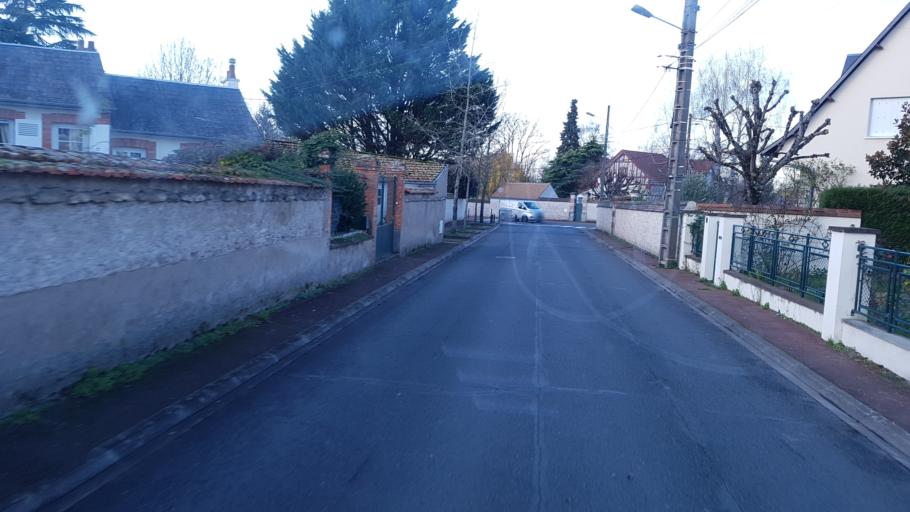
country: FR
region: Centre
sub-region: Departement du Loiret
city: Olivet
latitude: 47.8659
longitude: 1.9045
